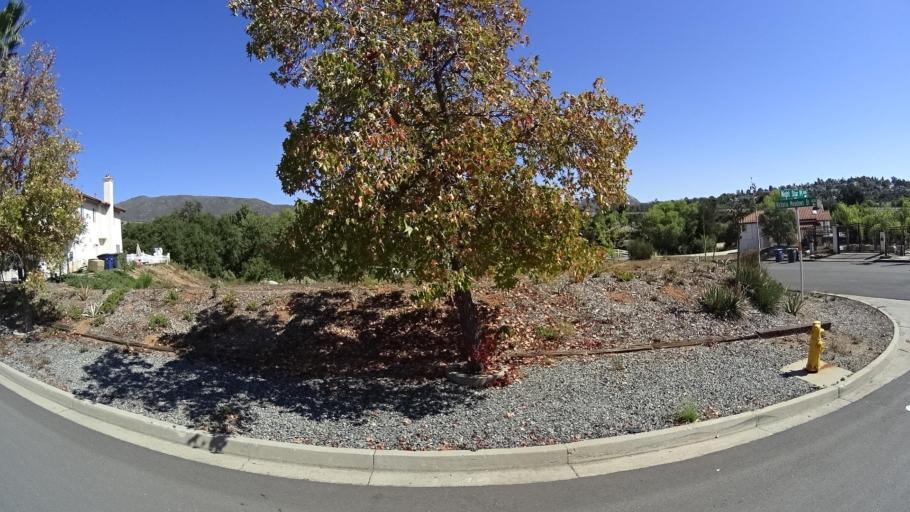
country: US
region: California
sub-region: San Diego County
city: Alpine
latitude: 32.8401
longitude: -116.7639
